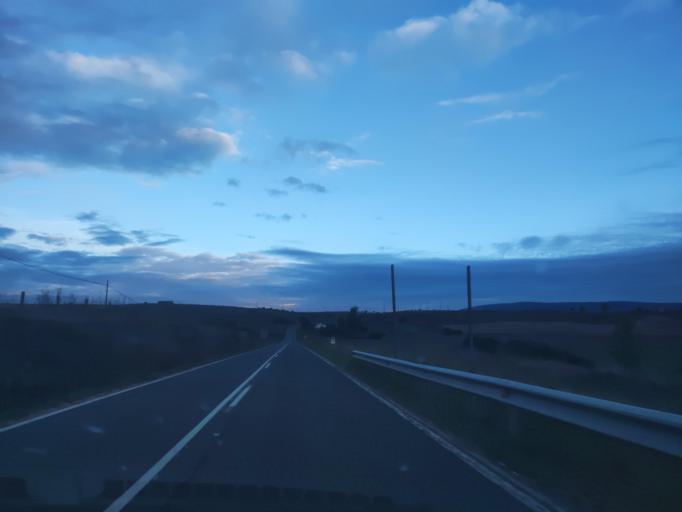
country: ES
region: Castille and Leon
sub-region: Provincia de Salamanca
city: Ciudad Rodrigo
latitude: 40.6108
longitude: -6.5345
